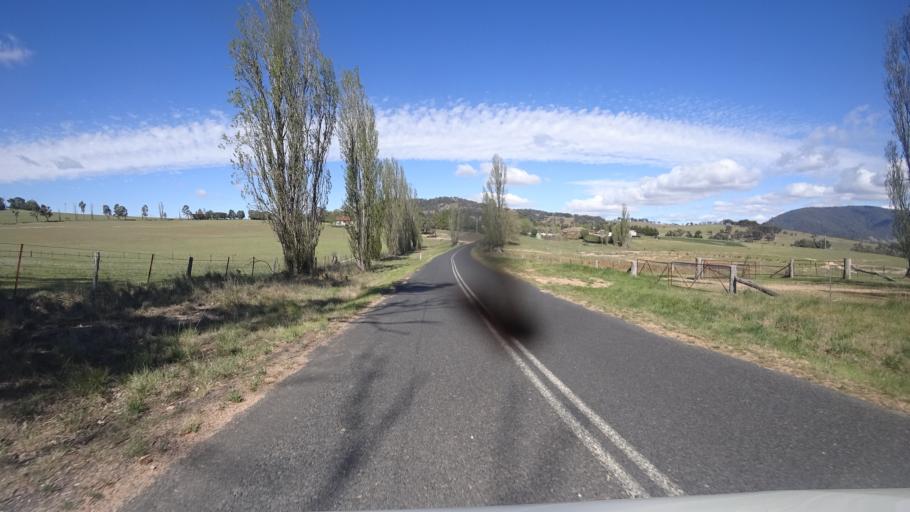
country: AU
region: New South Wales
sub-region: Lithgow
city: Portland
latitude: -33.5221
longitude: 149.9449
